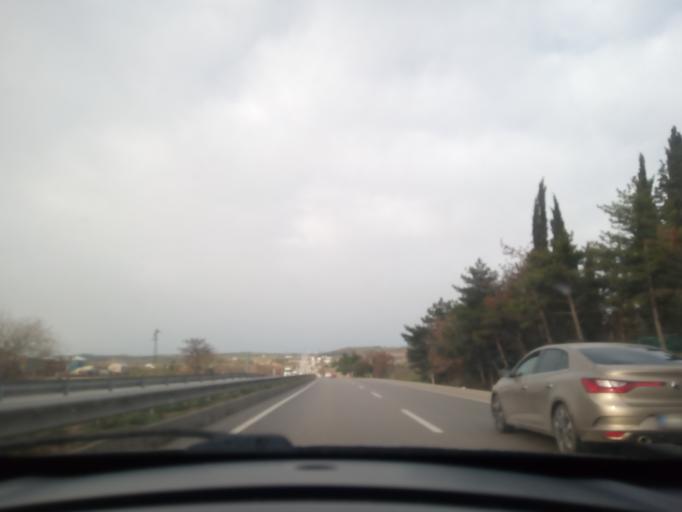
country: TR
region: Bursa
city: Gorukle
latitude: 40.2145
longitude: 28.7221
